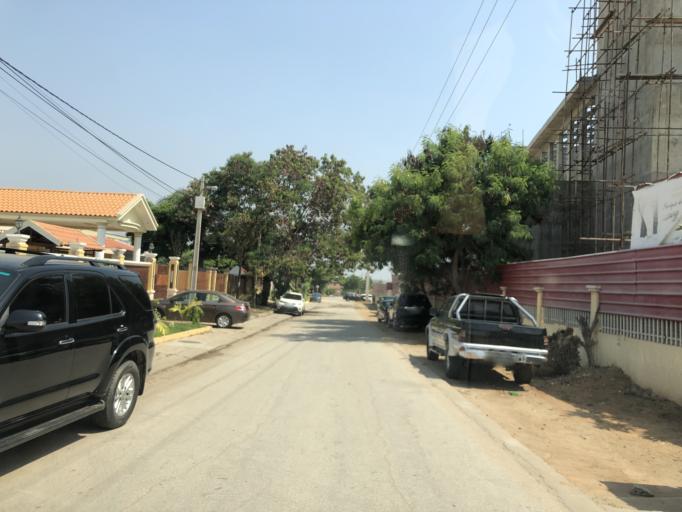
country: AO
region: Luanda
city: Luanda
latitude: -8.9026
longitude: 13.2314
